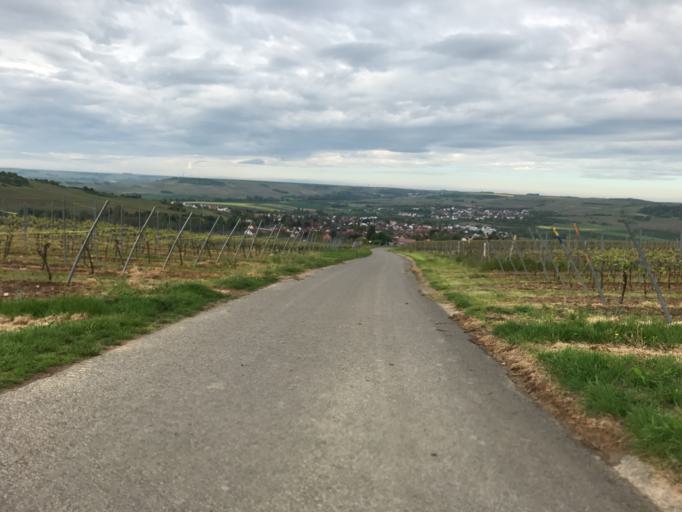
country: DE
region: Rheinland-Pfalz
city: Schwabenheim
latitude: 49.9391
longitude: 8.1032
